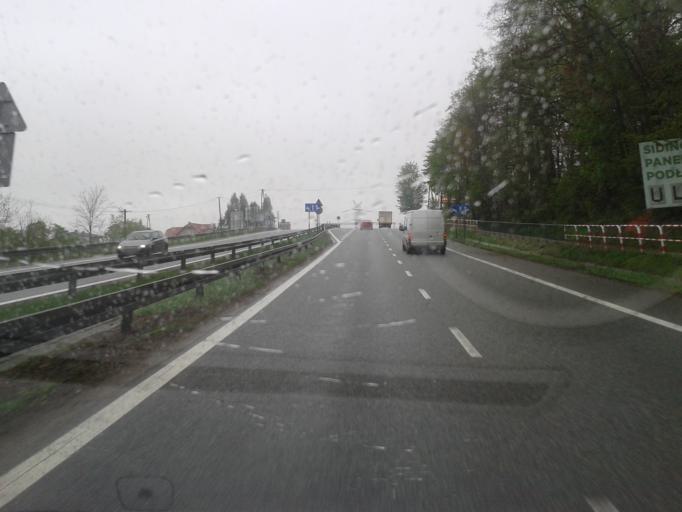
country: PL
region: Lesser Poland Voivodeship
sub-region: Powiat krakowski
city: Libertow
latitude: 49.9572
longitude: 19.8888
